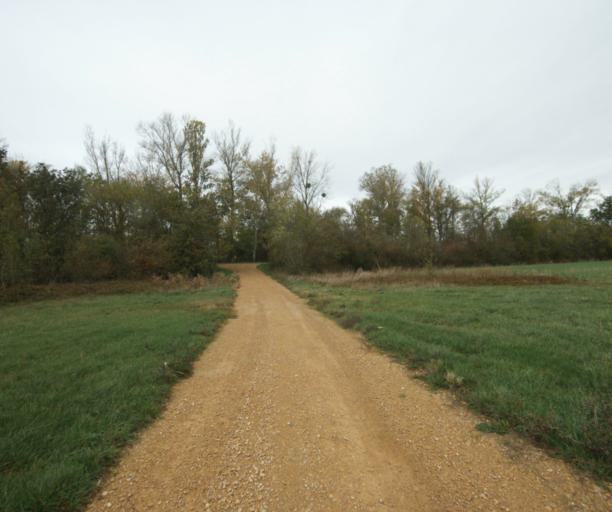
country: FR
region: Rhone-Alpes
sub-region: Departement de l'Ain
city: Pont-de-Vaux
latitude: 46.4582
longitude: 4.9023
